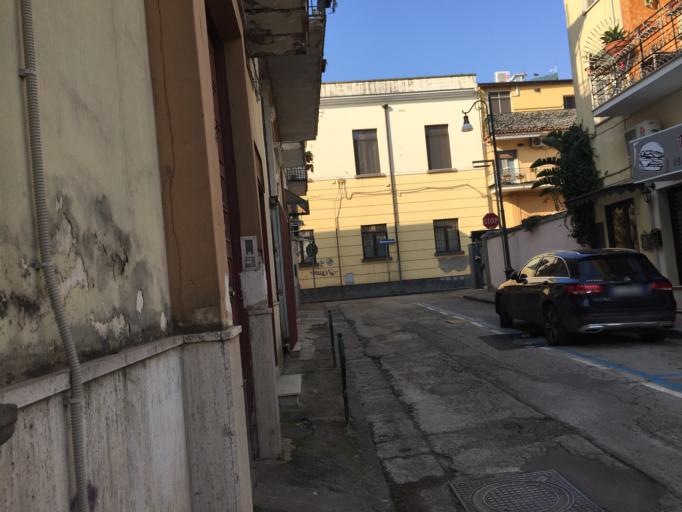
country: IT
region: Campania
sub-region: Provincia di Napoli
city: Pompei
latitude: 40.7487
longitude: 14.4983
